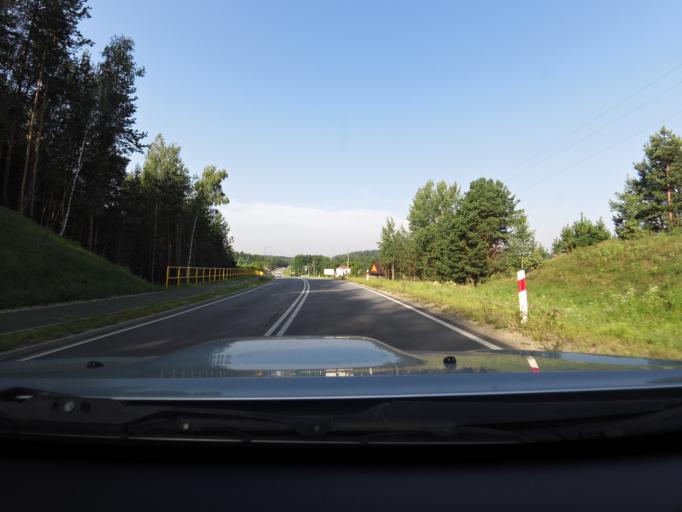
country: PL
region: Podlasie
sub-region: Powiat sejnenski
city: Krasnopol
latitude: 54.0834
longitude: 23.0985
